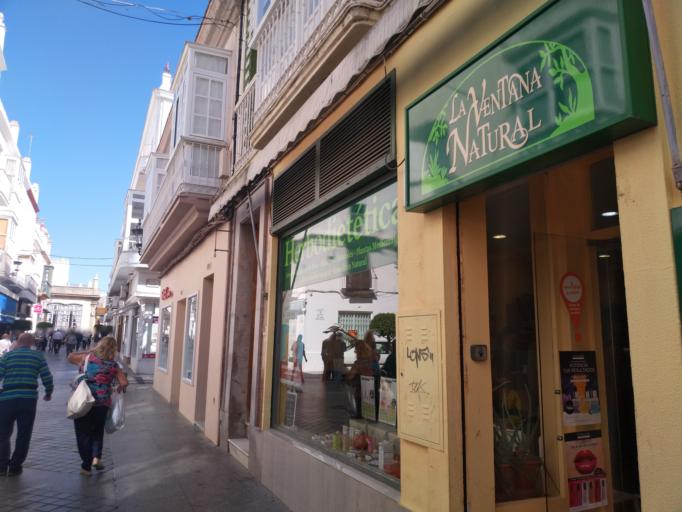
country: ES
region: Andalusia
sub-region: Provincia de Cadiz
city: San Fernando
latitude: 36.4676
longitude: -6.1961
